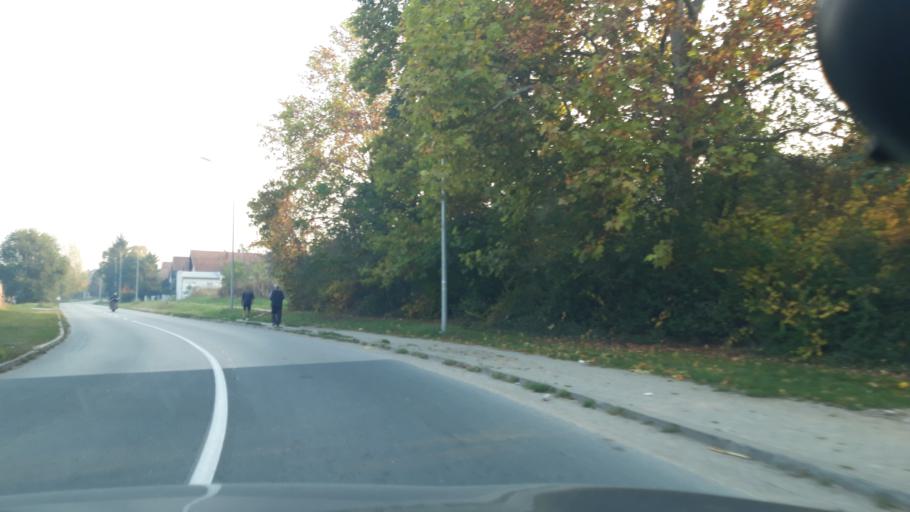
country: RS
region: Autonomna Pokrajina Vojvodina
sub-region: Sremski Okrug
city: Ingija
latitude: 45.0537
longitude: 20.0657
